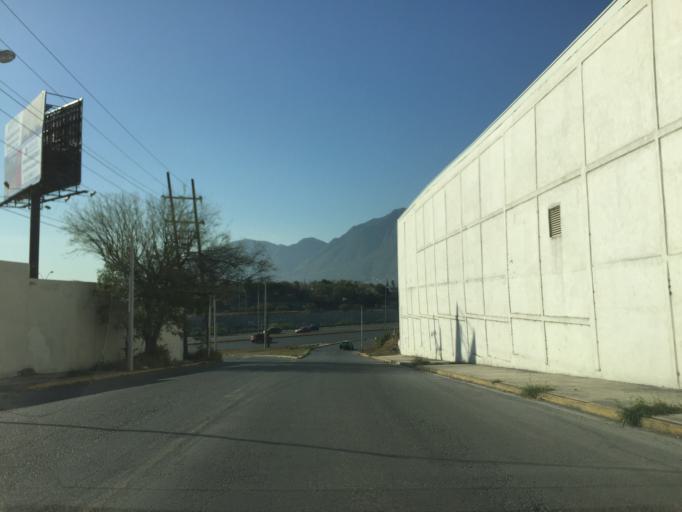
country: MX
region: Nuevo Leon
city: Guadalupe
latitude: 25.6923
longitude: -100.2173
